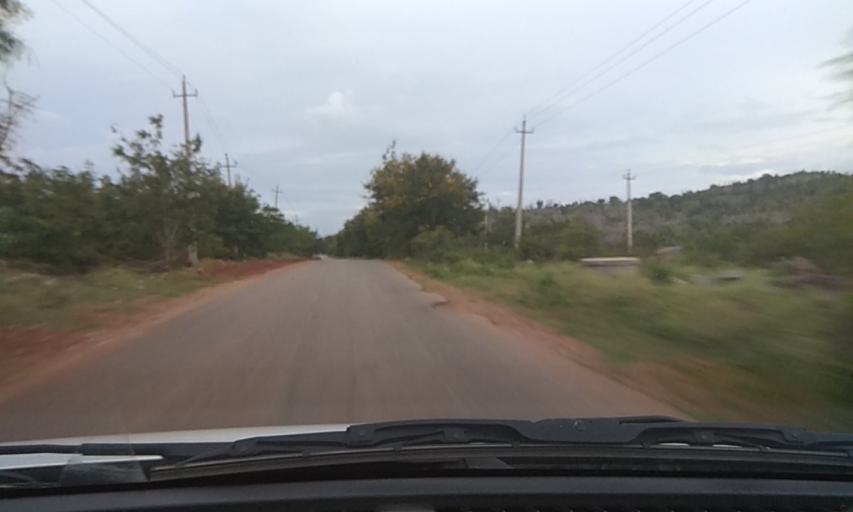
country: IN
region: Karnataka
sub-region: Chamrajnagar
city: Gundlupet
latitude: 11.7983
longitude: 76.7962
